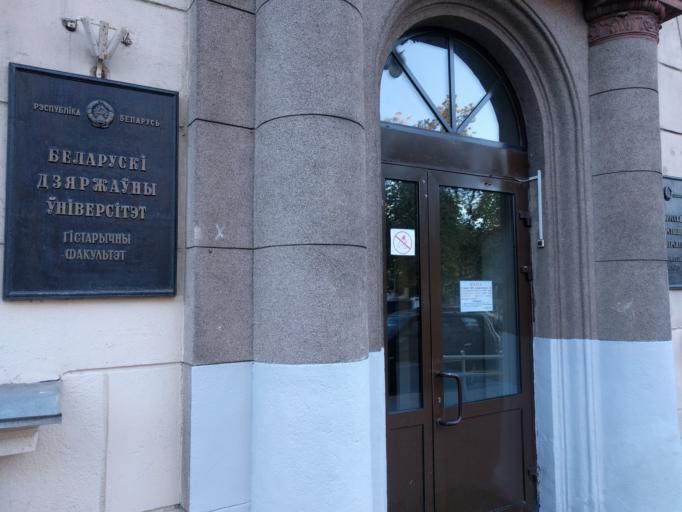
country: BY
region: Minsk
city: Minsk
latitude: 53.8999
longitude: 27.5669
